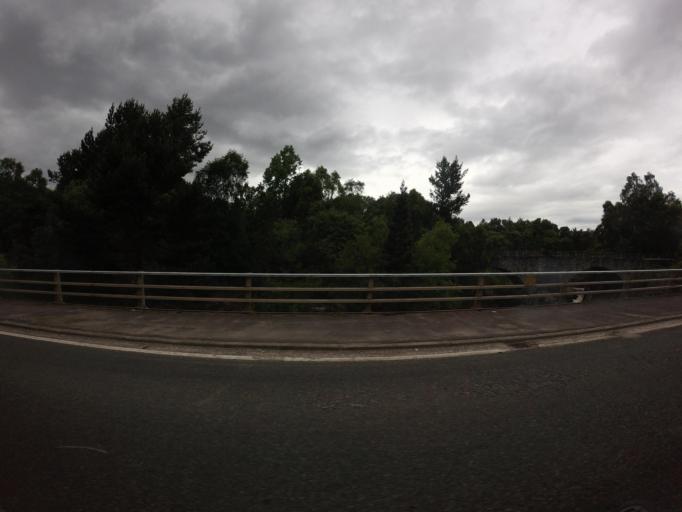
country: GB
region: Scotland
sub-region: Highland
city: Muir of Ord
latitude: 57.6364
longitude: -4.6773
